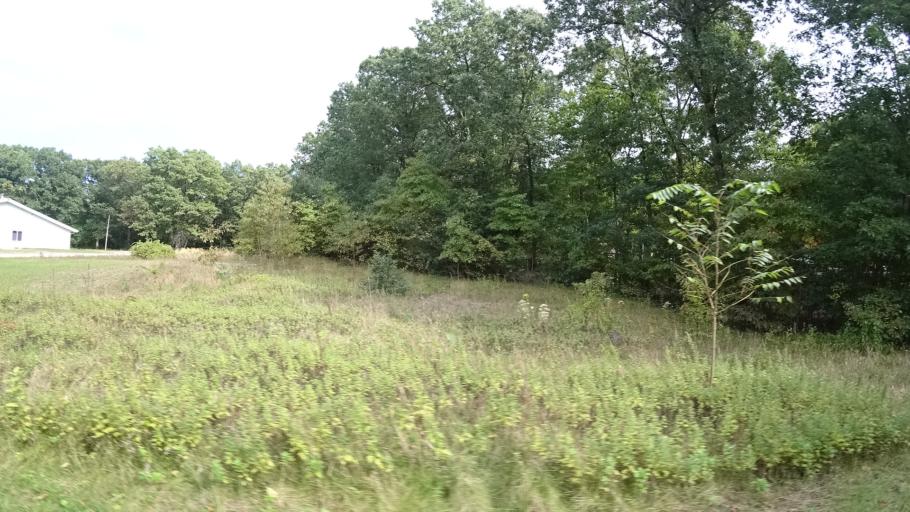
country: US
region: Indiana
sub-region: LaPorte County
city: Long Beach
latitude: 41.7336
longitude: -86.8471
